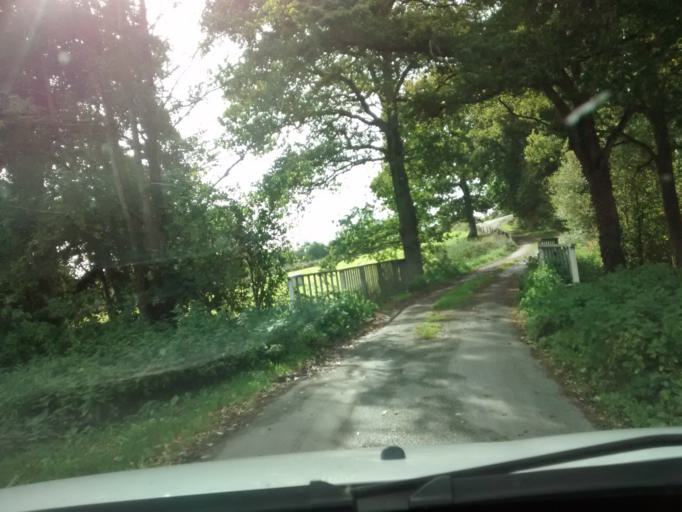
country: FR
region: Brittany
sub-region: Departement d'Ille-et-Vilaine
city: Poce-les-Bois
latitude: 48.1533
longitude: -1.3087
